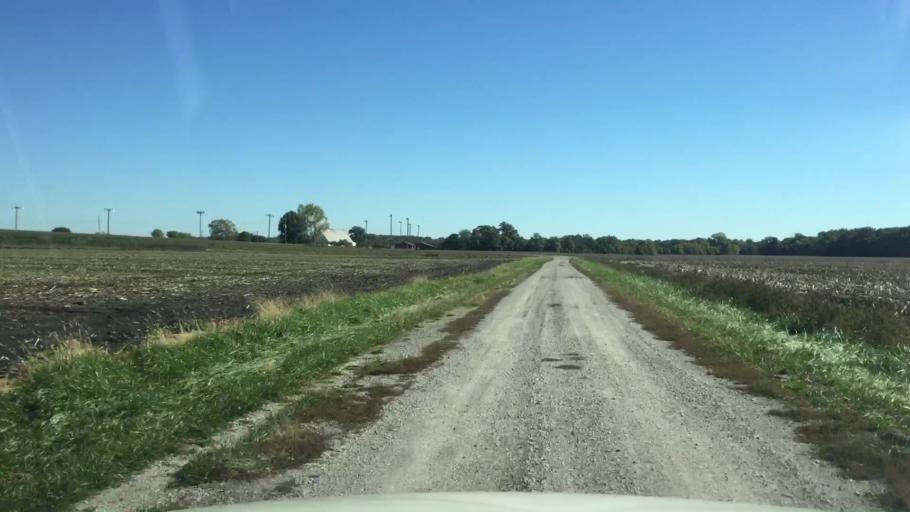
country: US
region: Kansas
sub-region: Douglas County
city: Eudora
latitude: 38.9315
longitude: -95.1518
